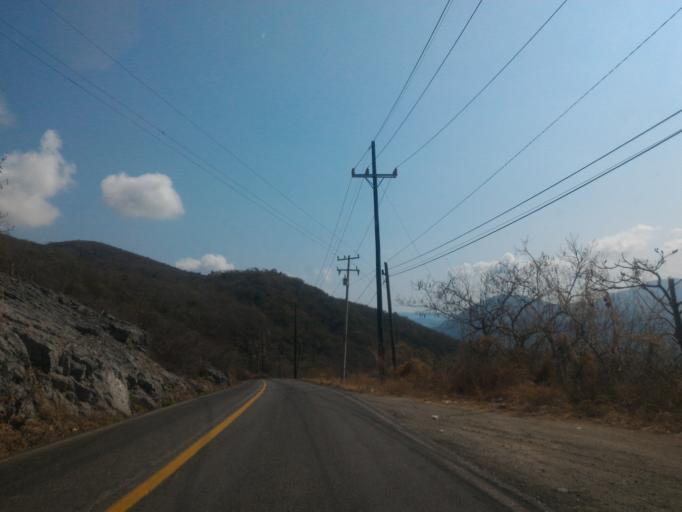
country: MX
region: Michoacan
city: Coahuayana Viejo
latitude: 18.5637
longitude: -103.6466
